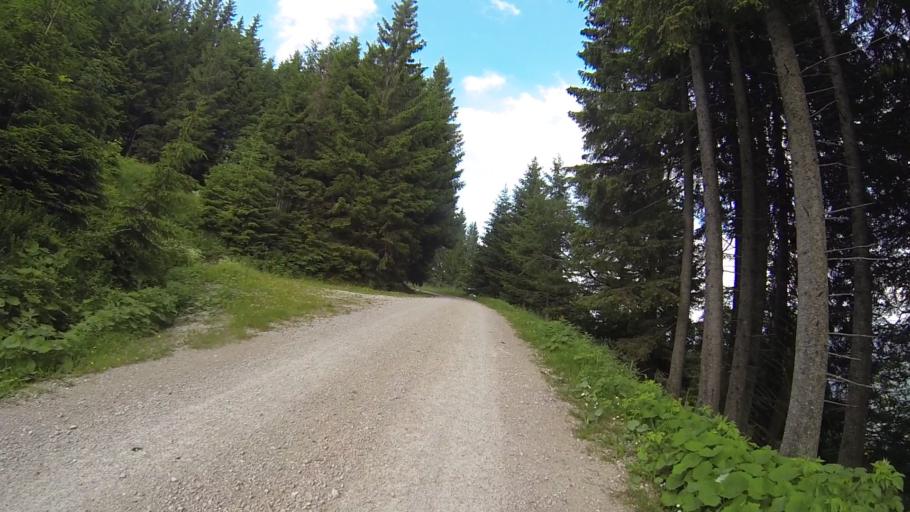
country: AT
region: Tyrol
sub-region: Politischer Bezirk Reutte
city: Jungholz
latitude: 47.5804
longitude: 10.4836
